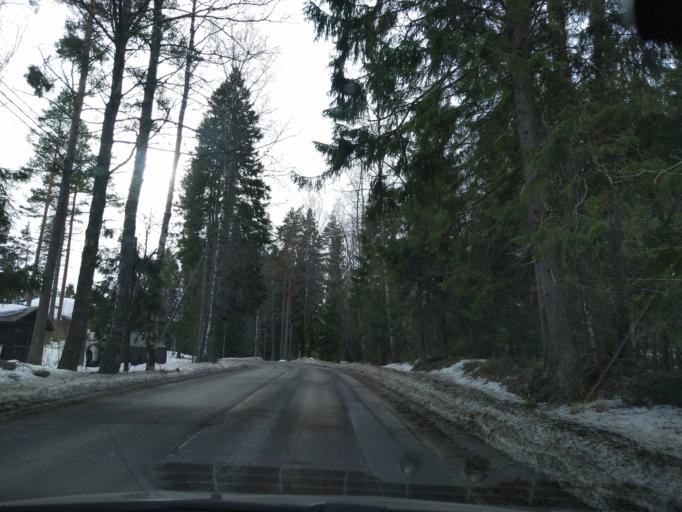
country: FI
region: Uusimaa
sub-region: Helsinki
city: Sibbo
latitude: 60.2635
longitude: 25.2867
